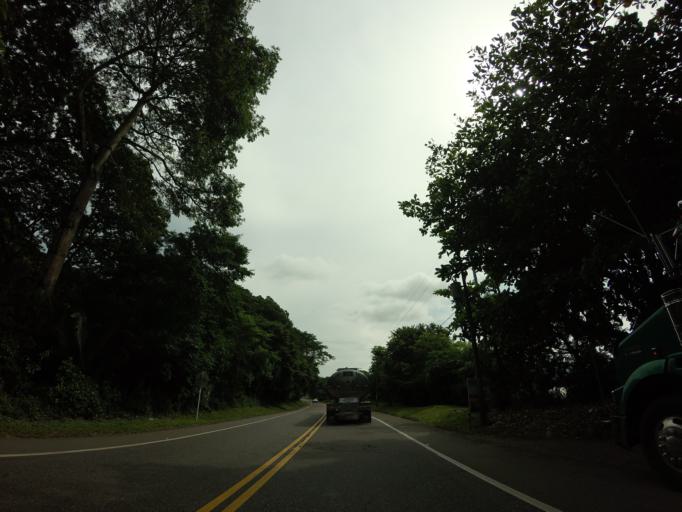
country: CO
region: Caldas
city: La Dorada
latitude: 5.4360
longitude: -74.6796
